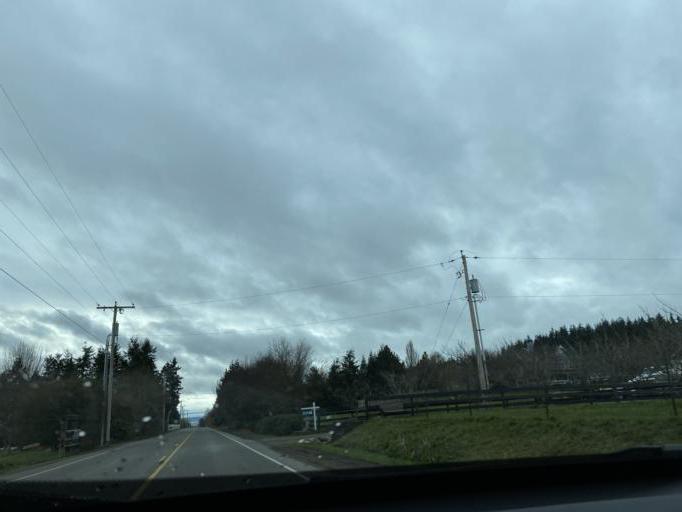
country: US
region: Washington
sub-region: Island County
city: Freeland
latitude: 48.0039
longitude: -122.5072
